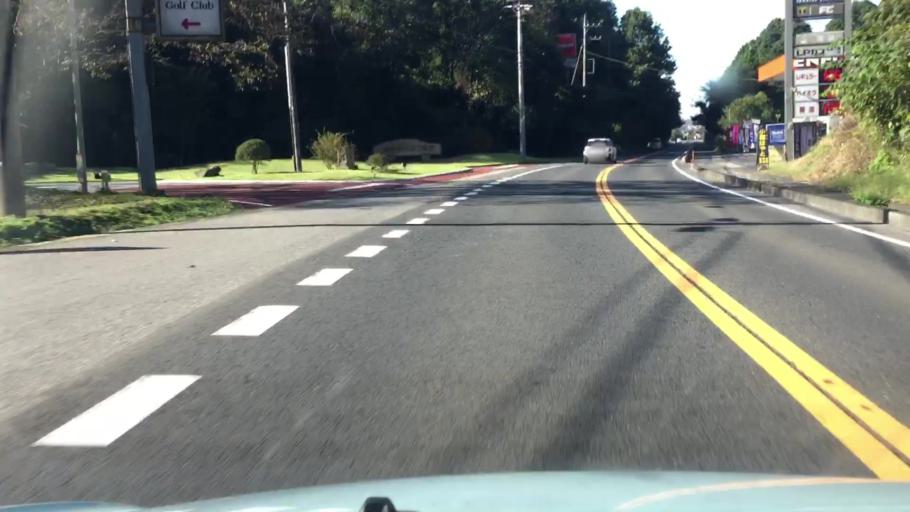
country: JP
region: Tochigi
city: Ujiie
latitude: 36.7004
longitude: 140.0155
